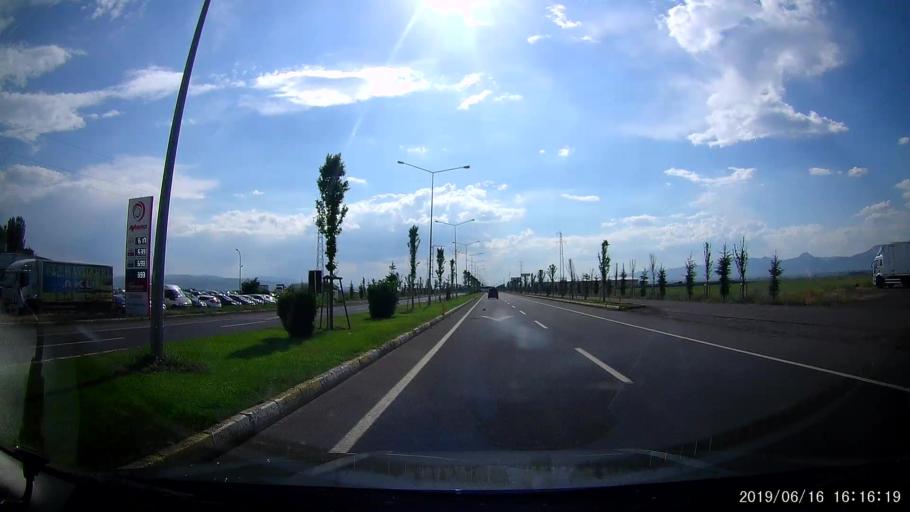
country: TR
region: Erzurum
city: Erzurum
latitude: 39.9628
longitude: 41.2084
